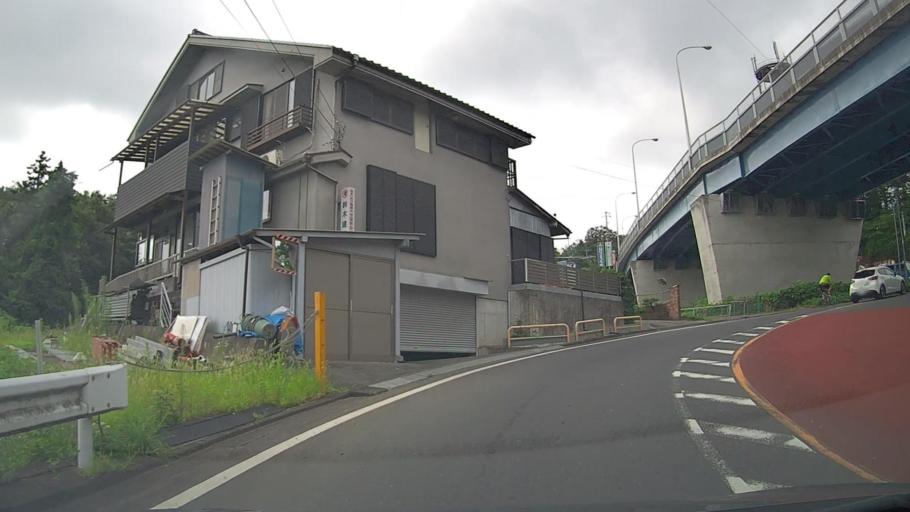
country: JP
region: Tokyo
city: Itsukaichi
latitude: 35.7217
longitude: 139.2567
